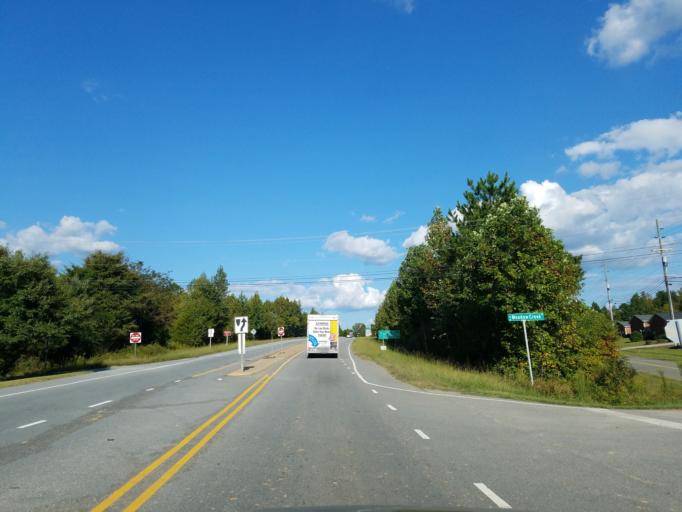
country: US
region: North Carolina
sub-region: Davidson County
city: Lexington
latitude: 35.8004
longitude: -80.2978
